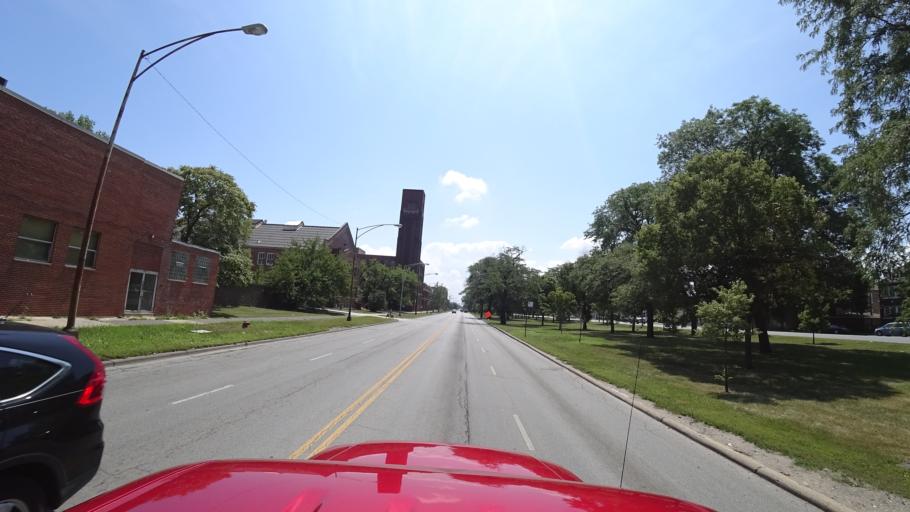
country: US
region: Illinois
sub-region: Cook County
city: Chicago
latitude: 41.8149
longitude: -87.6841
